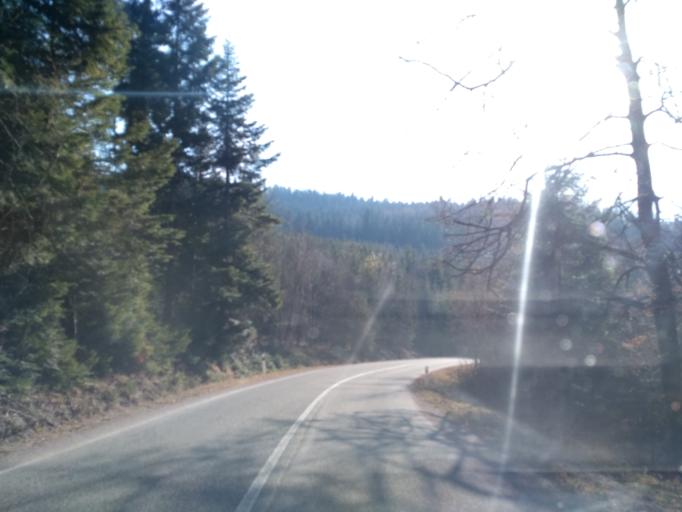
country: SK
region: Kosicky
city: Medzev
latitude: 48.7225
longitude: 20.7486
